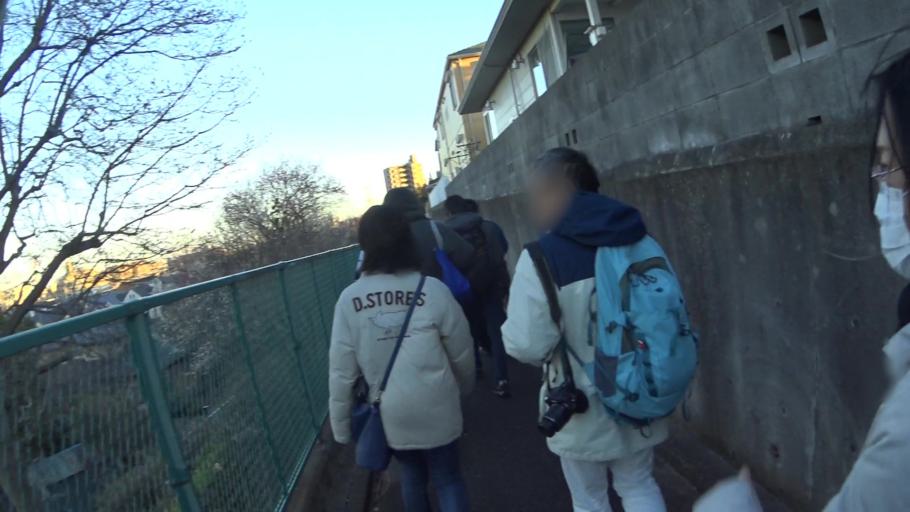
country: JP
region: Saitama
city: Koshigaya
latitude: 35.8827
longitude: 139.7365
